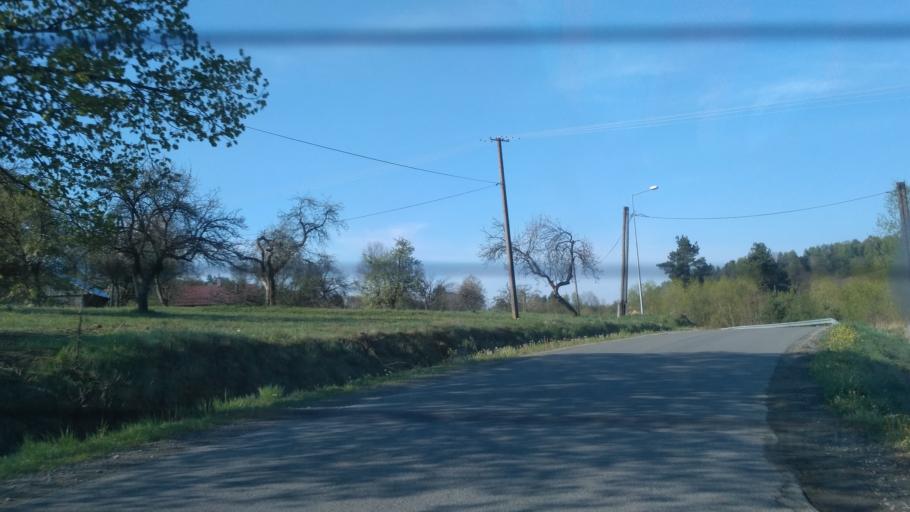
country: PL
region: Subcarpathian Voivodeship
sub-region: Powiat jaroslawski
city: Kramarzowka
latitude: 49.8236
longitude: 22.4975
